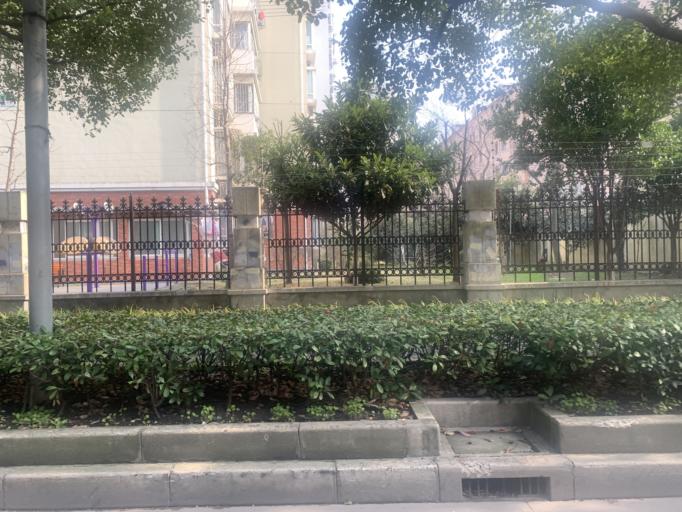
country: CN
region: Shanghai Shi
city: Huamu
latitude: 31.1853
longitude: 121.5147
